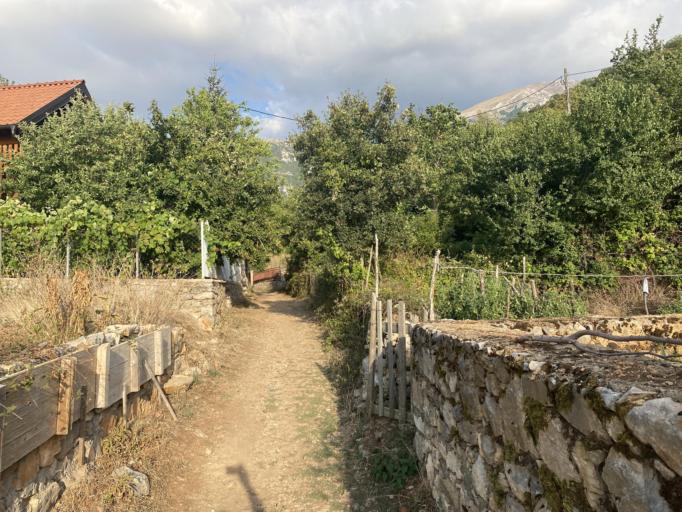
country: AL
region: Korce
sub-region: Rrethi i Pogradecit
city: Bucimas
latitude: 40.9580
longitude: 20.7785
